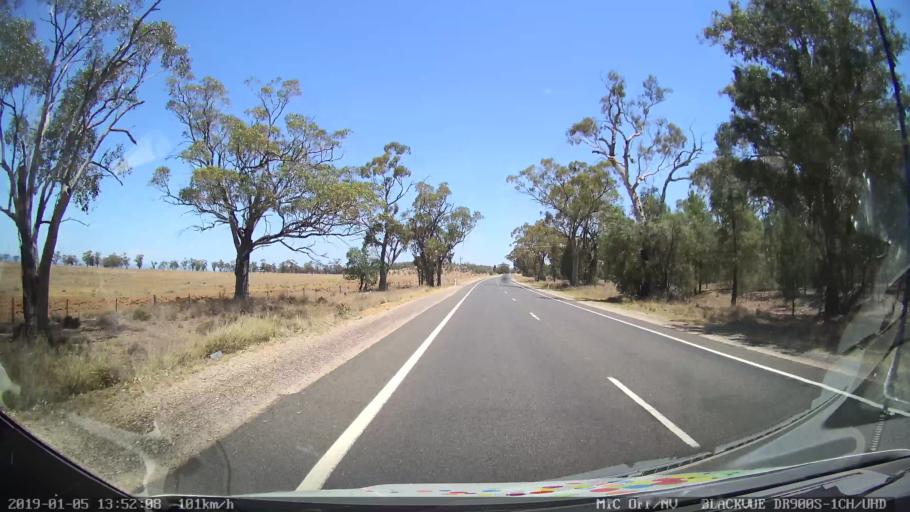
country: AU
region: New South Wales
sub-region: Gunnedah
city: Gunnedah
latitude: -31.0551
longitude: 150.2779
